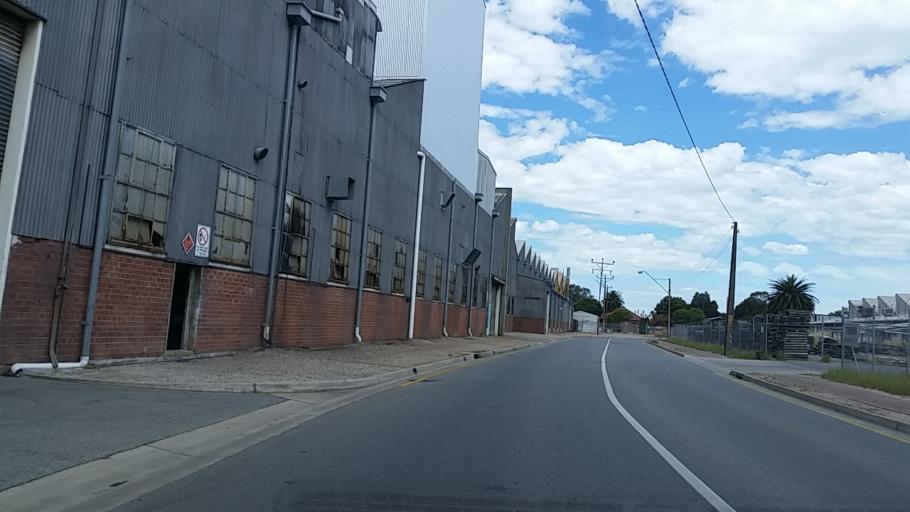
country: AU
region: South Australia
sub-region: Charles Sturt
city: Woodville North
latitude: -34.8639
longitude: 138.5384
